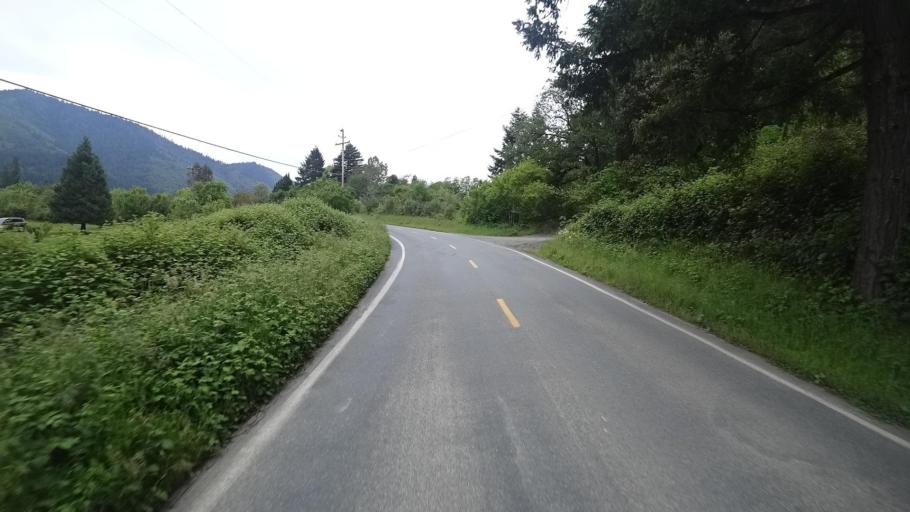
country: US
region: California
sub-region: Humboldt County
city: Willow Creek
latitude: 41.0576
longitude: -123.6886
